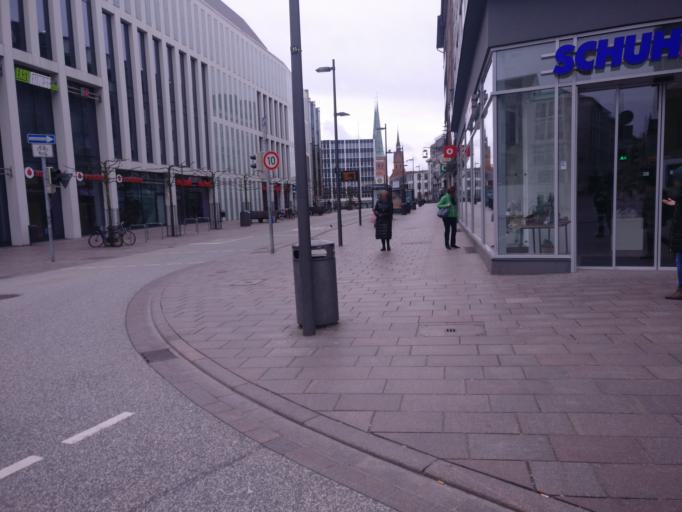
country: DE
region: Schleswig-Holstein
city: Luebeck
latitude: 53.8659
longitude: 10.6850
